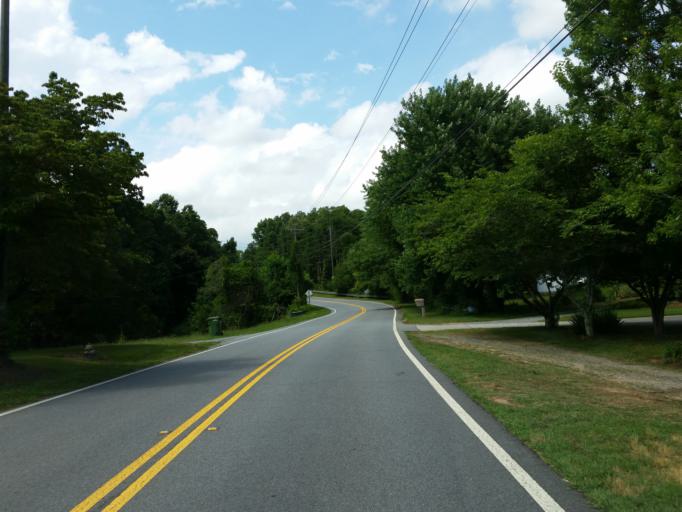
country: US
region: Georgia
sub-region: Fulton County
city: Roswell
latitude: 34.0567
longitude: -84.4355
